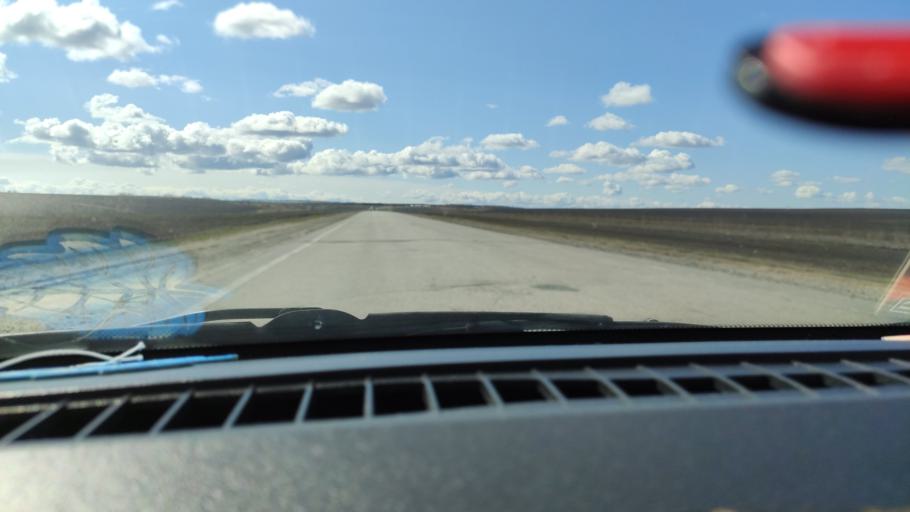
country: RU
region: Samara
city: Varlamovo
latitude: 53.0141
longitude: 48.3326
